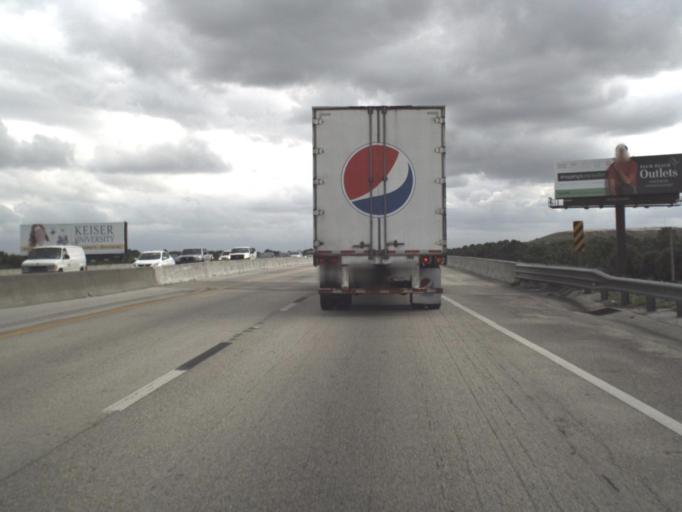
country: US
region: Florida
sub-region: Palm Beach County
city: Palm Beach Gardens
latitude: 26.7966
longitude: -80.1317
